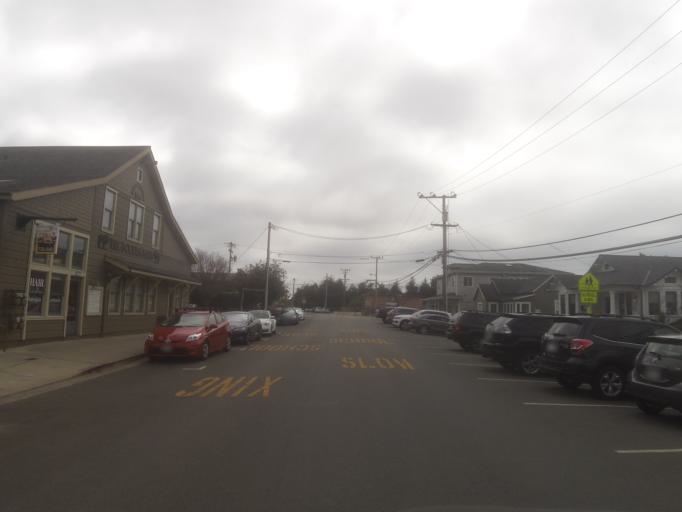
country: US
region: California
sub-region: San Mateo County
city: Half Moon Bay
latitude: 37.4625
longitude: -122.4304
